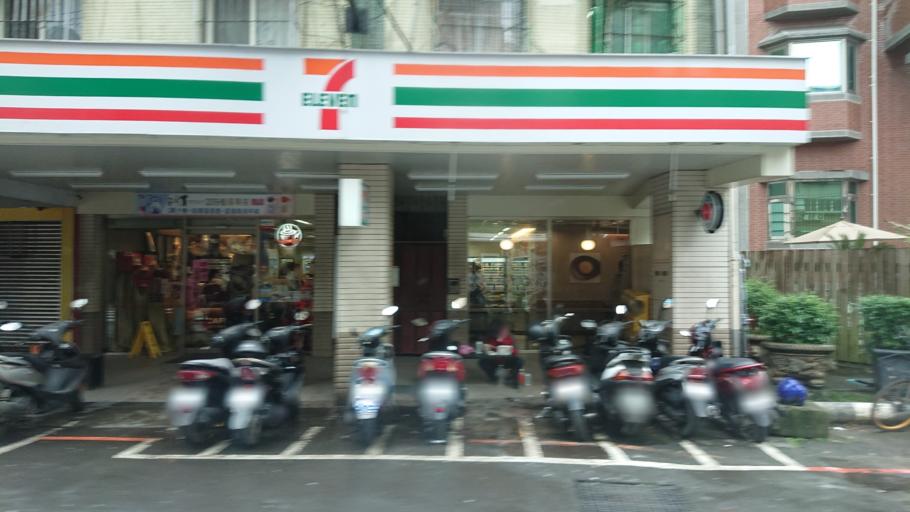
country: TW
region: Taipei
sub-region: Taipei
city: Banqiao
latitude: 24.9830
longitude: 121.4614
